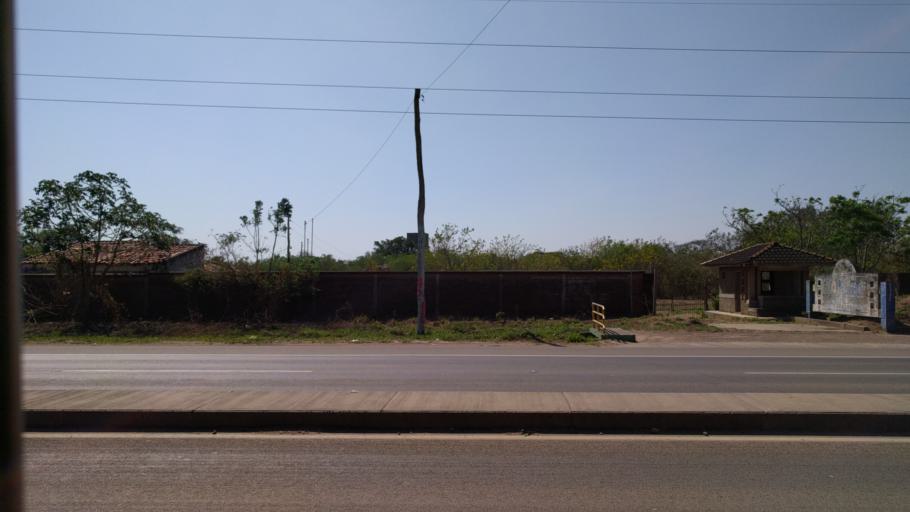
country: BO
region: Santa Cruz
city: Cotoca
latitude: -17.7663
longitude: -63.0464
